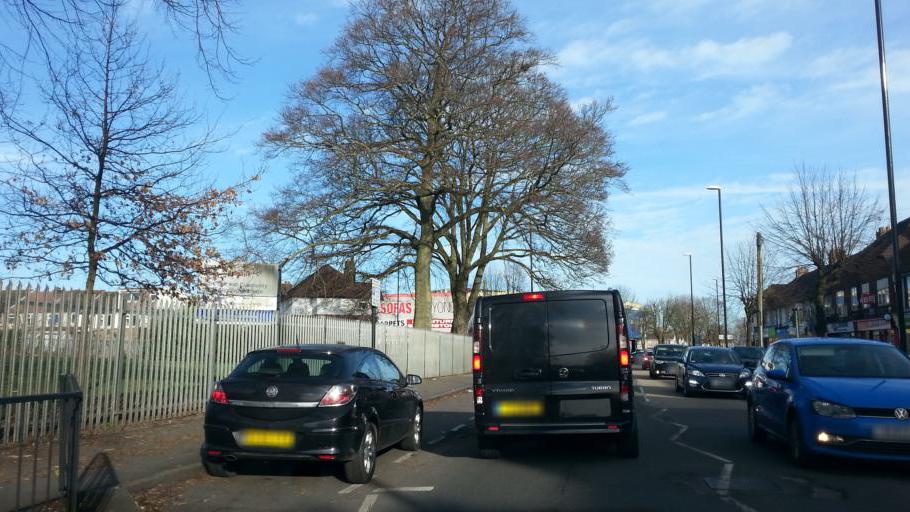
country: GB
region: England
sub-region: Coventry
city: Coventry
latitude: 52.4113
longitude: -1.4739
